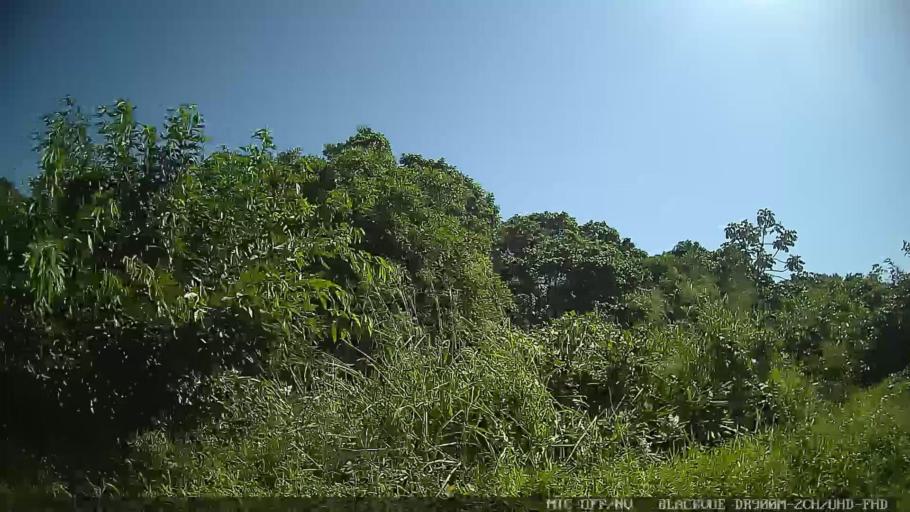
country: BR
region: Sao Paulo
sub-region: Itanhaem
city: Itanhaem
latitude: -24.2109
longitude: -46.8584
